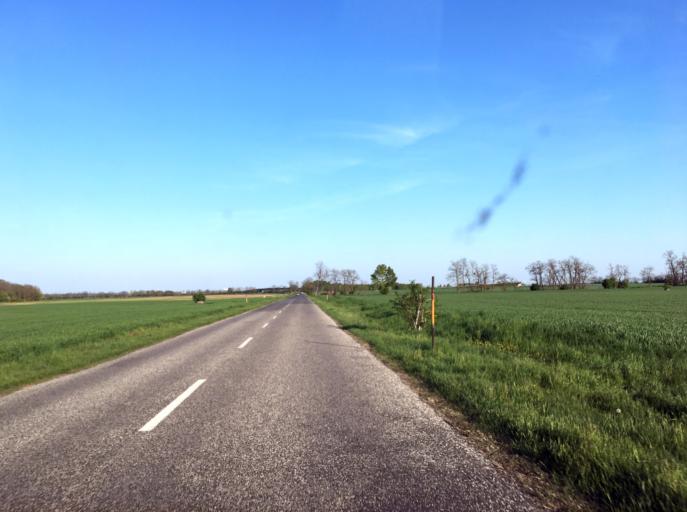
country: AT
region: Burgenland
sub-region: Politischer Bezirk Neusiedl am See
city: Kittsee
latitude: 48.0770
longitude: 17.0822
